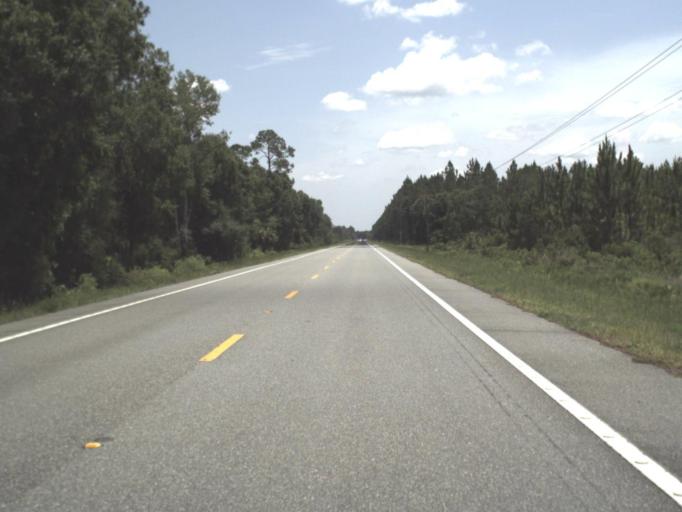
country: US
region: Florida
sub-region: Taylor County
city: Steinhatchee
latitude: 29.7680
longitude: -83.3383
